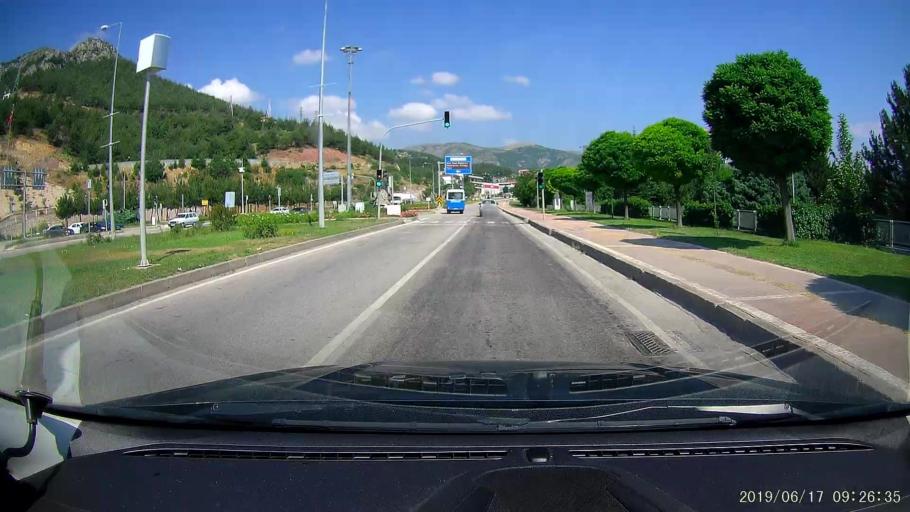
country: TR
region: Amasya
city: Amasya
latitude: 40.6702
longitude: 35.8342
